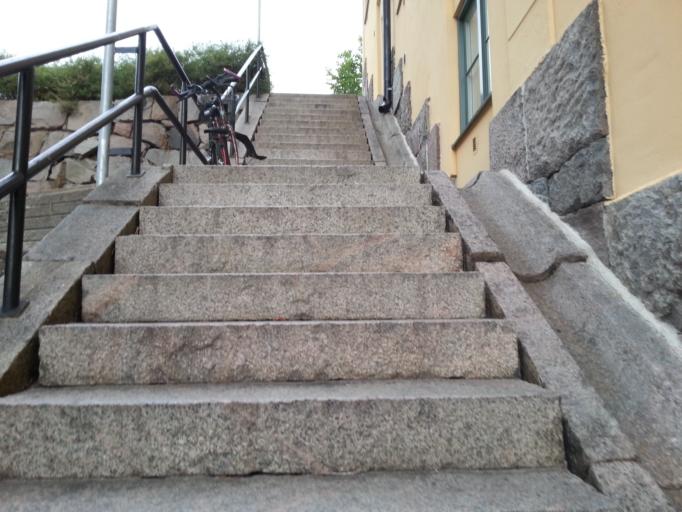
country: SE
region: OEstergoetland
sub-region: Norrkopings Kommun
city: Norrkoping
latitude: 58.5894
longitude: 16.1731
